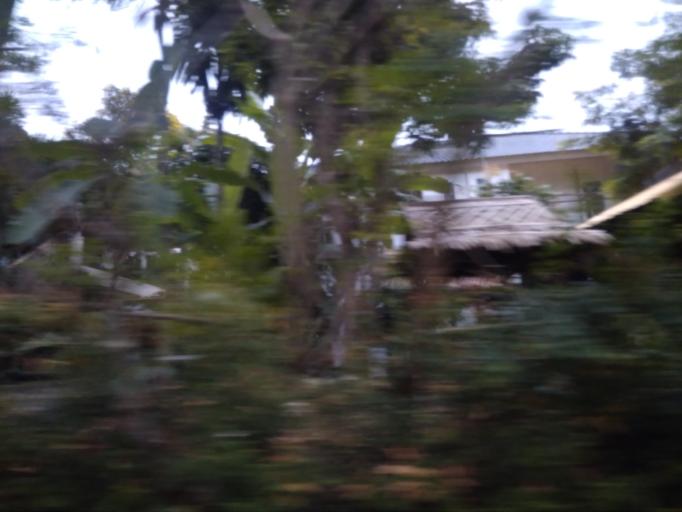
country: TH
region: Phuket
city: Mueang Phuket
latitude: 7.8149
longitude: 98.3960
